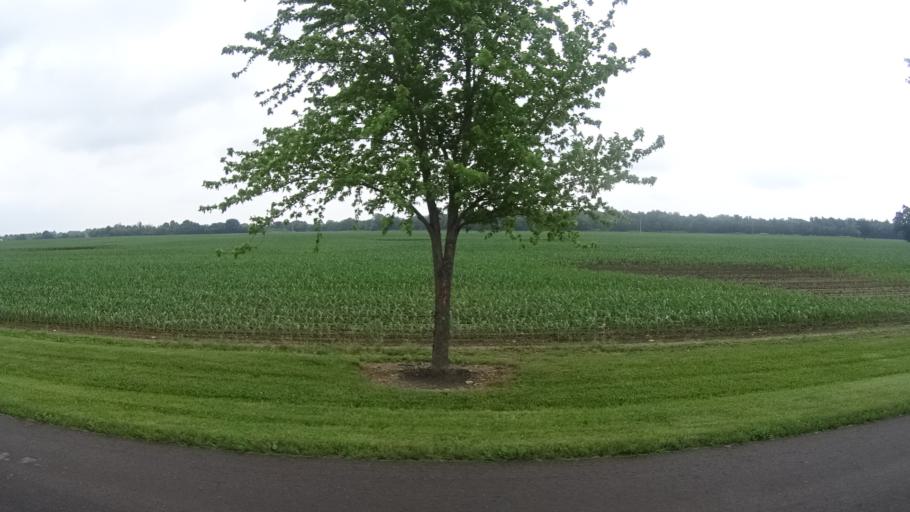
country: US
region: Ohio
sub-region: Huron County
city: Bellevue
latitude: 41.3567
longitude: -82.7857
